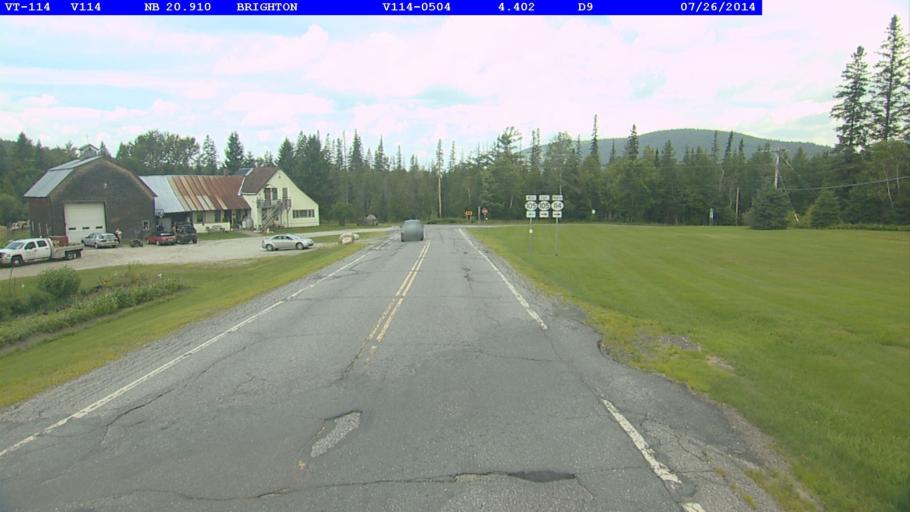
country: US
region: Vermont
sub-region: Caledonia County
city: Lyndonville
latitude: 44.7966
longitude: -71.9110
